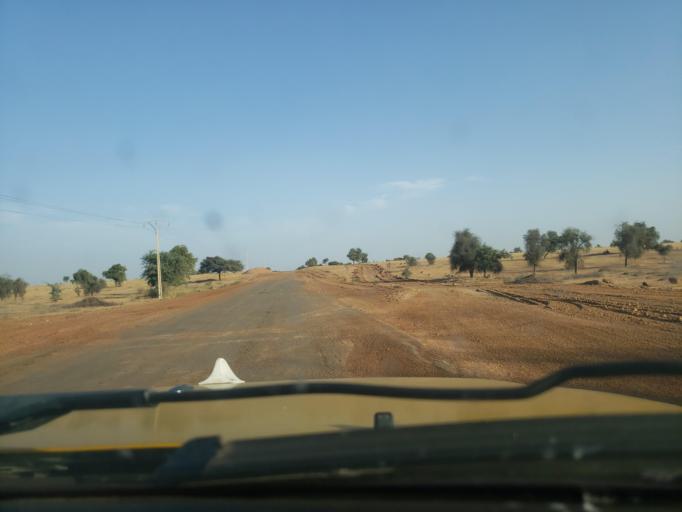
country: SN
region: Louga
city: Dara
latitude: 15.4279
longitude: -15.7439
